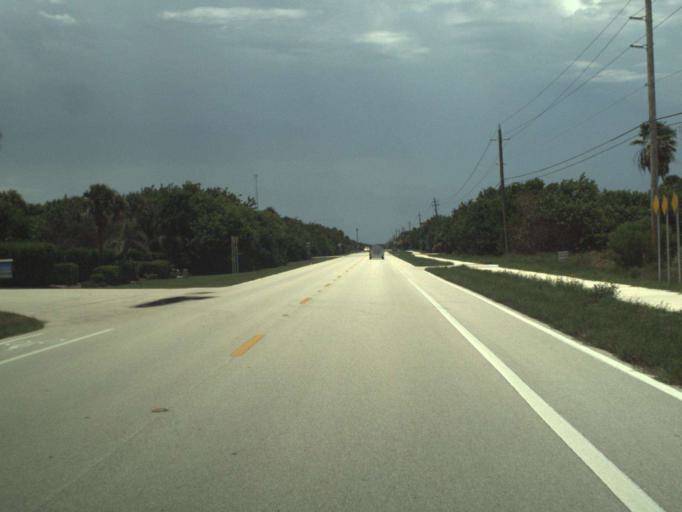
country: US
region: Florida
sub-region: Saint Lucie County
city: Hutchinson Island South
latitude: 27.3242
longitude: -80.2293
